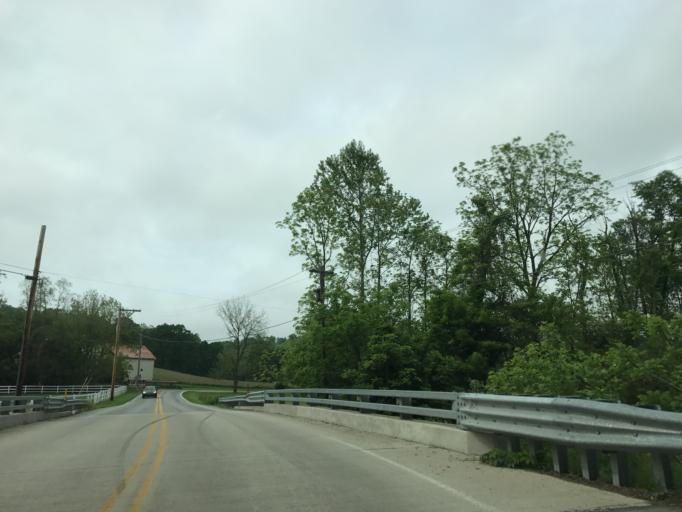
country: US
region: Pennsylvania
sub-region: York County
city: Susquehanna Trails
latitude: 39.7827
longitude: -76.4072
